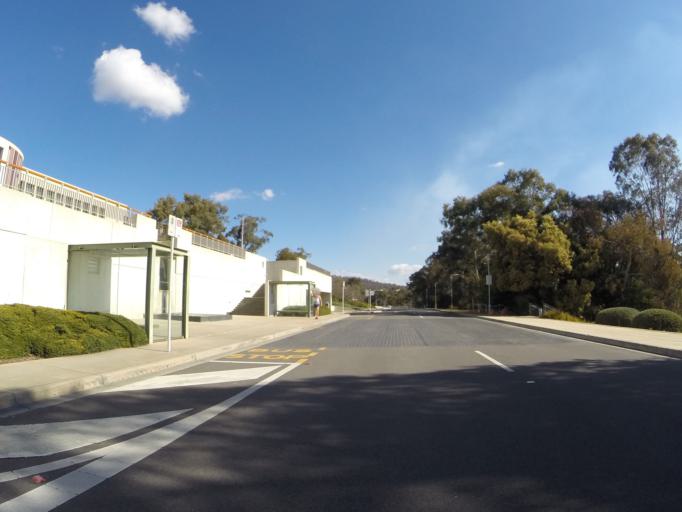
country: AU
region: Australian Capital Territory
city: Forrest
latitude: -35.3070
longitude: 149.1230
